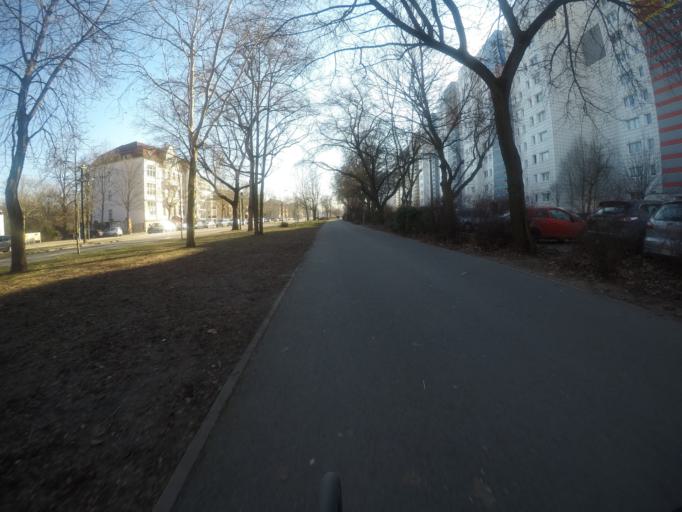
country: DE
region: Berlin
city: Friedrichsfelde
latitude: 52.5032
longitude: 13.5205
